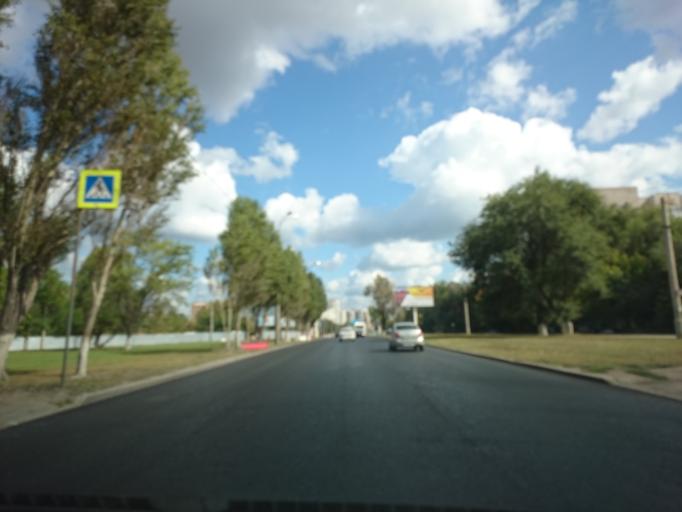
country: RU
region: Samara
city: Samara
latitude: 53.2314
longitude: 50.1818
